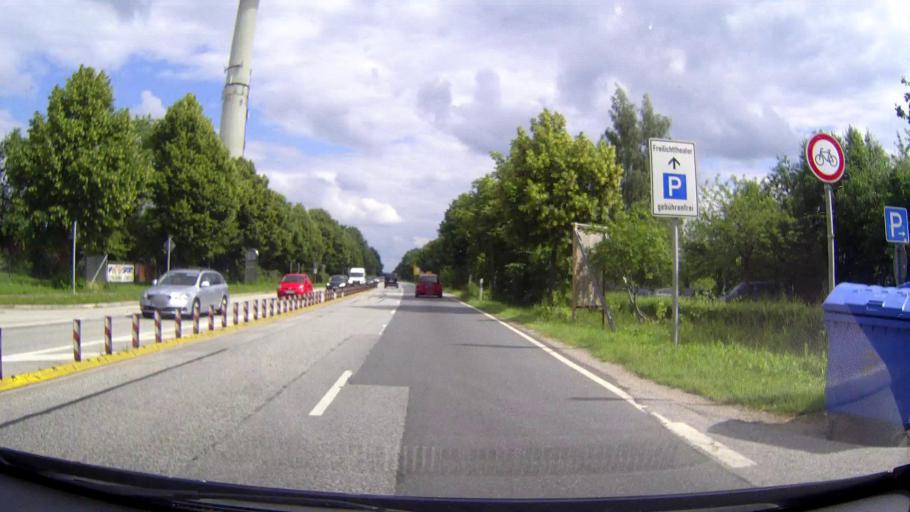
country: DE
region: Schleswig-Holstein
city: Bad Segeberg
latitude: 53.9321
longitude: 10.3119
